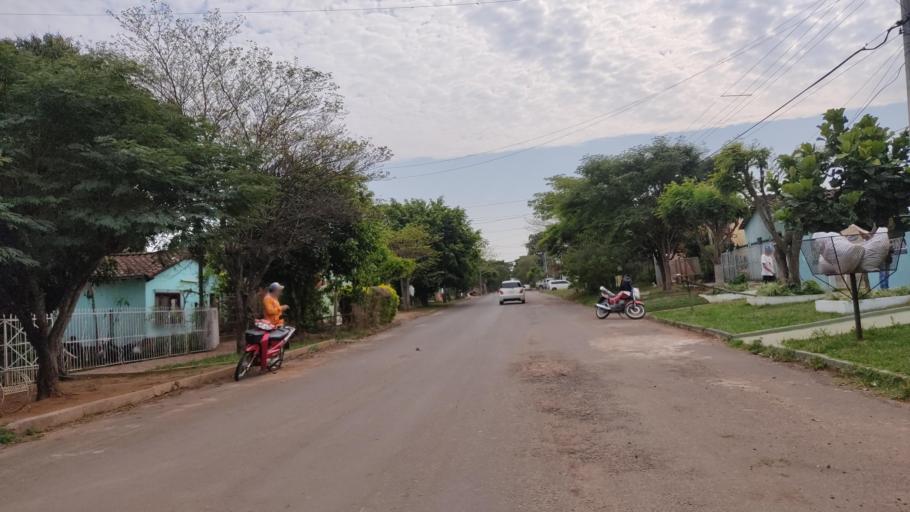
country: PY
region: Misiones
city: San Juan Bautista
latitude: -26.6714
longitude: -57.1519
